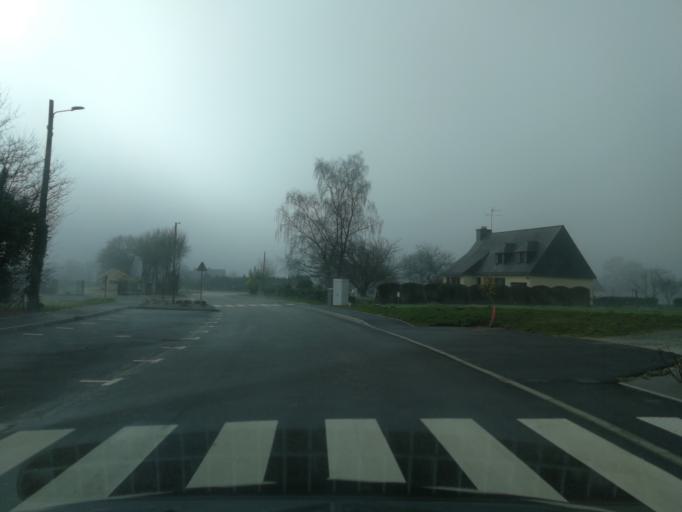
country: FR
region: Brittany
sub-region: Departement du Morbihan
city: La Vraie-Croix
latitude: 47.7401
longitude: -2.5017
